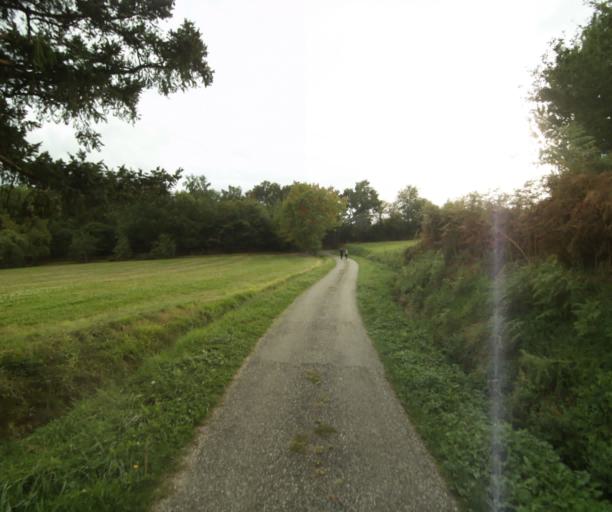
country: FR
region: Midi-Pyrenees
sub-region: Departement du Gers
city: Eauze
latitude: 43.9525
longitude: 0.0959
